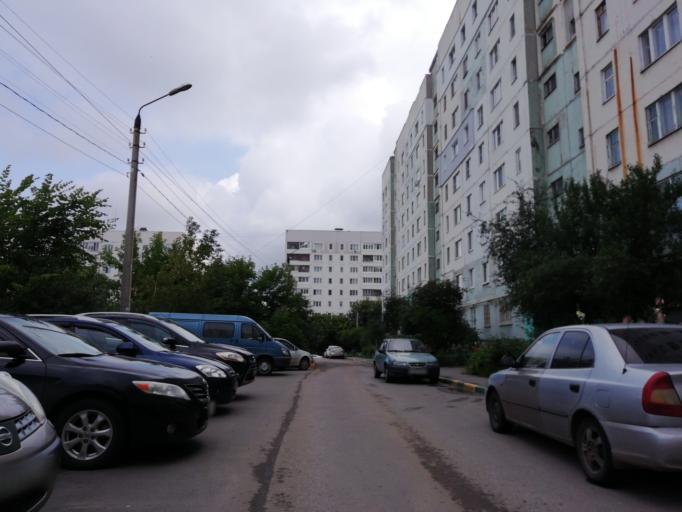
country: RU
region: Tula
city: Tula
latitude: 54.2031
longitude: 37.6468
